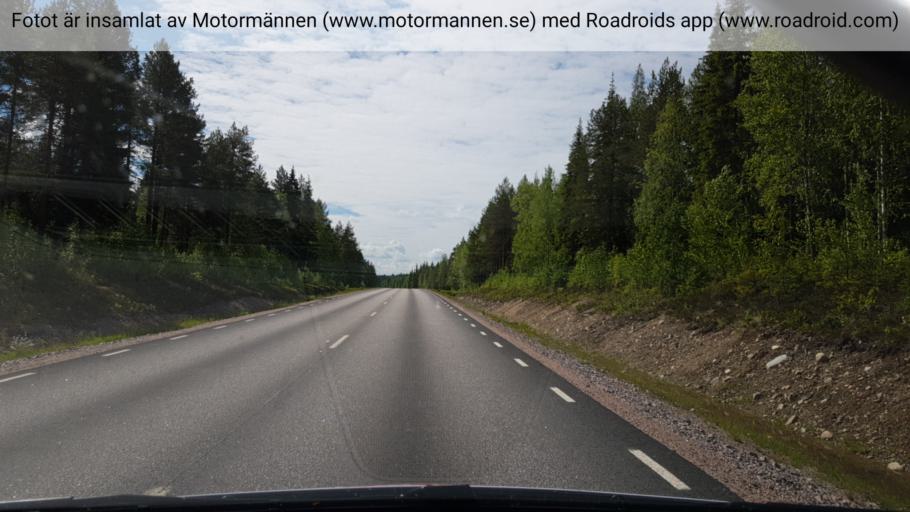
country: SE
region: Norrbotten
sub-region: Overtornea Kommun
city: OEvertornea
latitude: 66.5026
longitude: 23.7187
